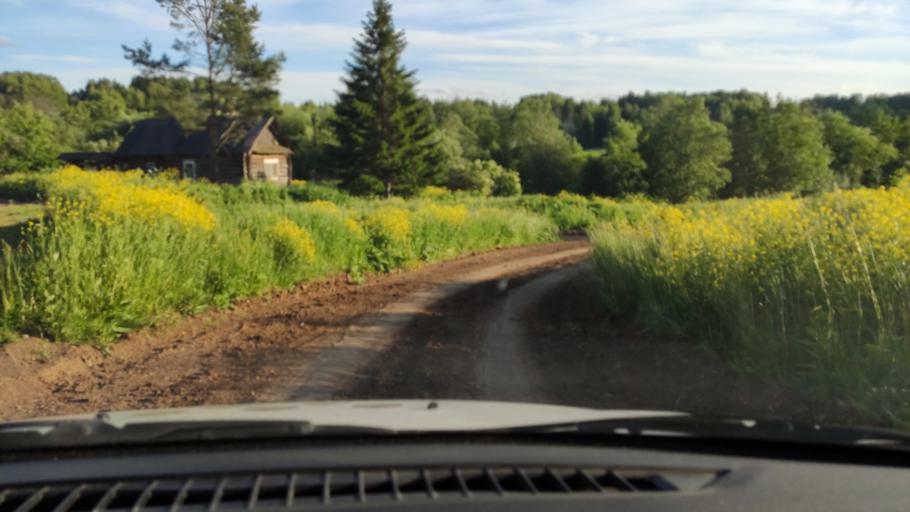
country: RU
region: Perm
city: Orda
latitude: 57.2916
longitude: 56.5933
